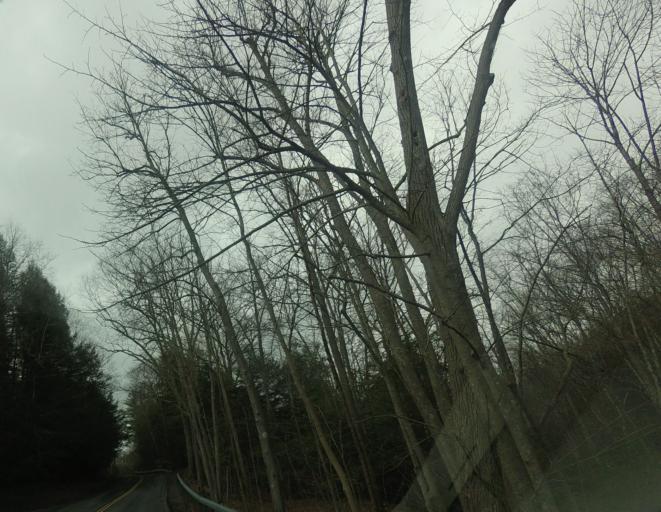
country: US
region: New York
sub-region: Tompkins County
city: Northwest Ithaca
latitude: 42.4376
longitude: -76.5499
